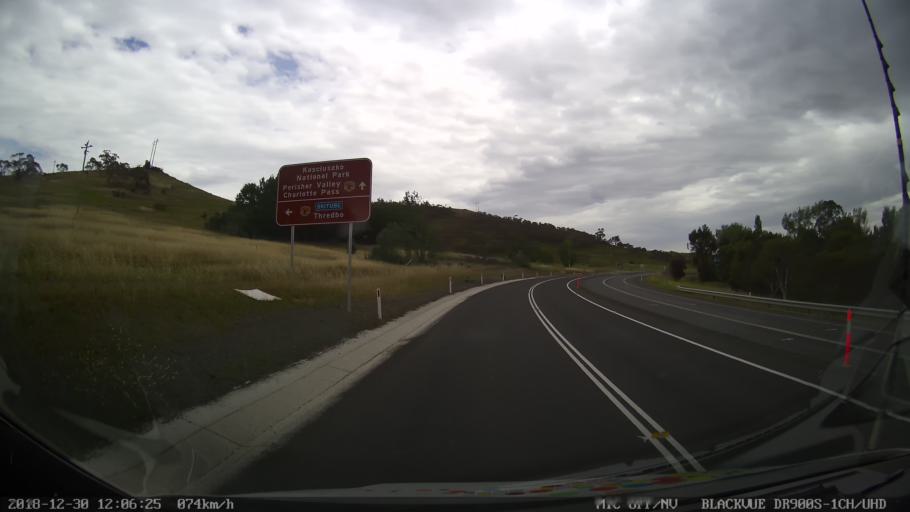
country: AU
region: New South Wales
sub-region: Snowy River
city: Jindabyne
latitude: -36.4126
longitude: 148.5945
